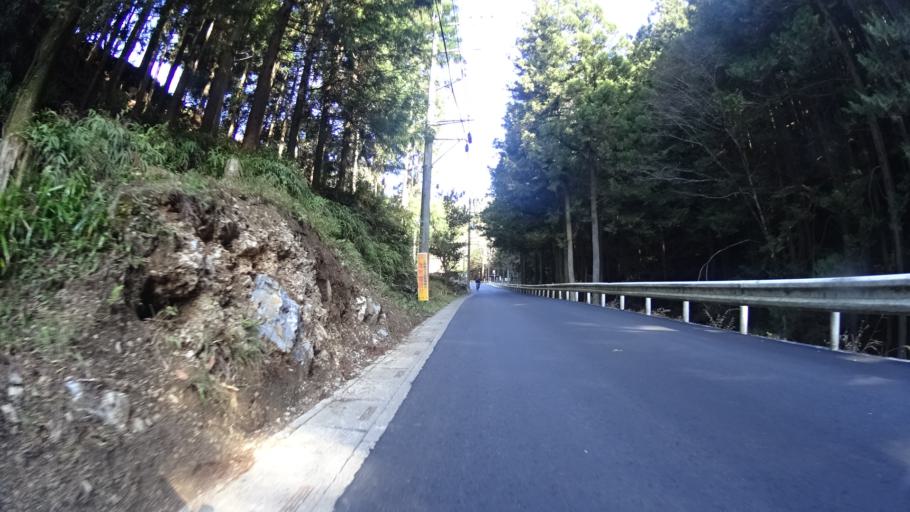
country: JP
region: Saitama
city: Chichibu
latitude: 35.9194
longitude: 139.1507
